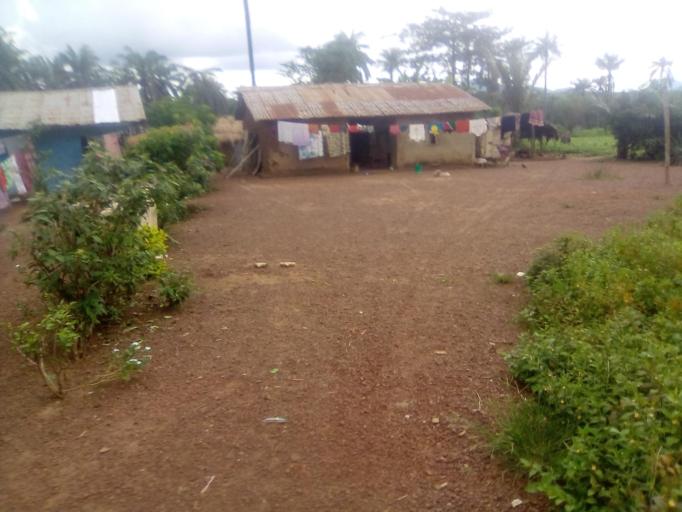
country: SL
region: Southern Province
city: Moyamba
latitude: 8.1473
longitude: -12.4361
